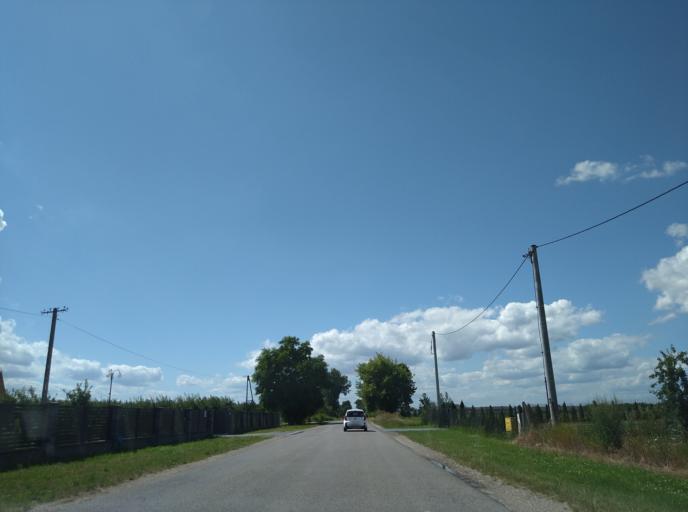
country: PL
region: Masovian Voivodeship
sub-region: Powiat bialobrzeski
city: Bialobrzegi
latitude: 51.6708
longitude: 20.9004
